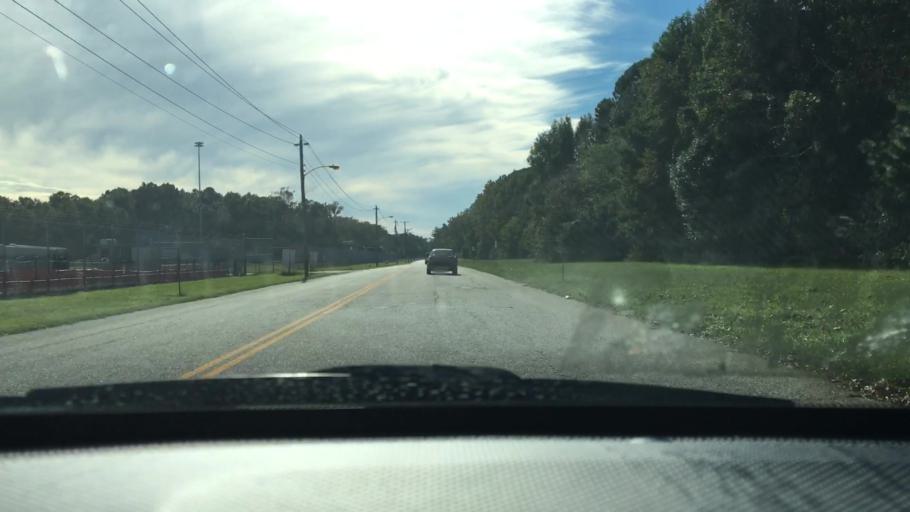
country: US
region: Virginia
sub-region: City of Portsmouth
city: Portsmouth Heights
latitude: 36.8793
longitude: -76.3631
